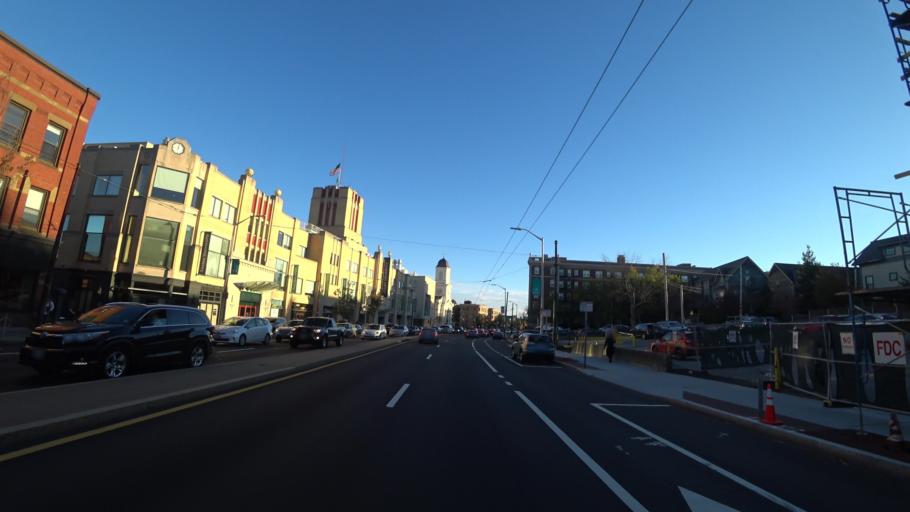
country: US
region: Massachusetts
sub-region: Middlesex County
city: Cambridge
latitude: 42.3879
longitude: -71.1194
